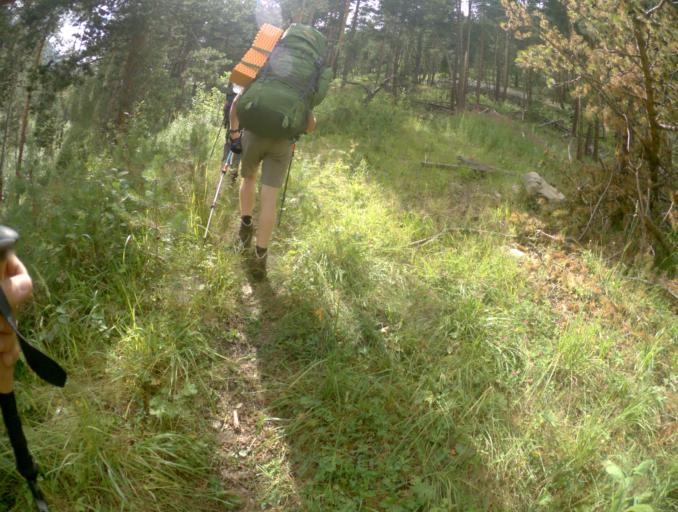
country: RU
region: Karachayevo-Cherkesiya
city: Uchkulan
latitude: 43.3458
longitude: 42.1493
